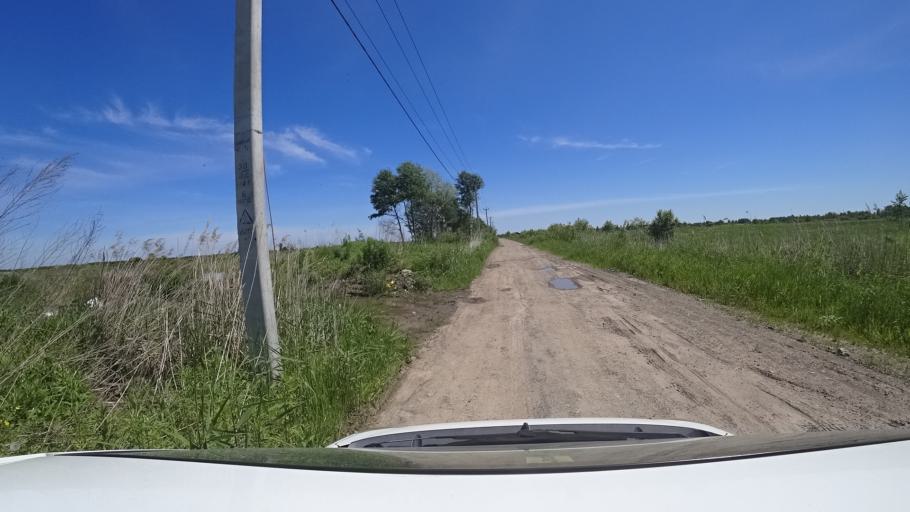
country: RU
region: Khabarovsk Krai
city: Topolevo
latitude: 48.5001
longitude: 135.1988
